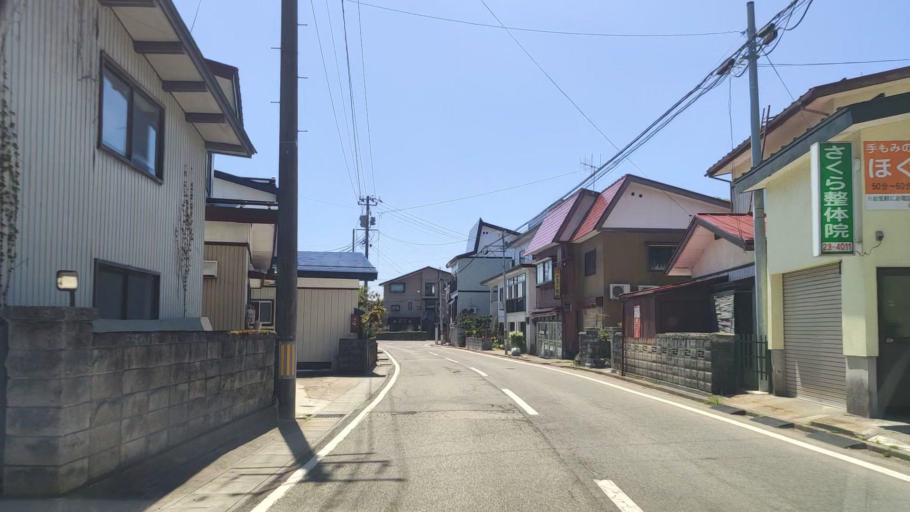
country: JP
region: Yamagata
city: Shinjo
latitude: 38.7735
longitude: 140.3082
